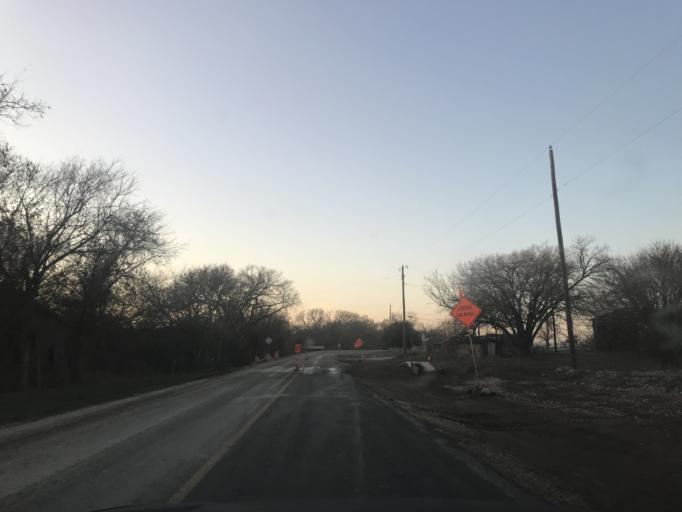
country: US
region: Texas
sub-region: Williamson County
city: Hutto
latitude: 30.5046
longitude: -97.5191
